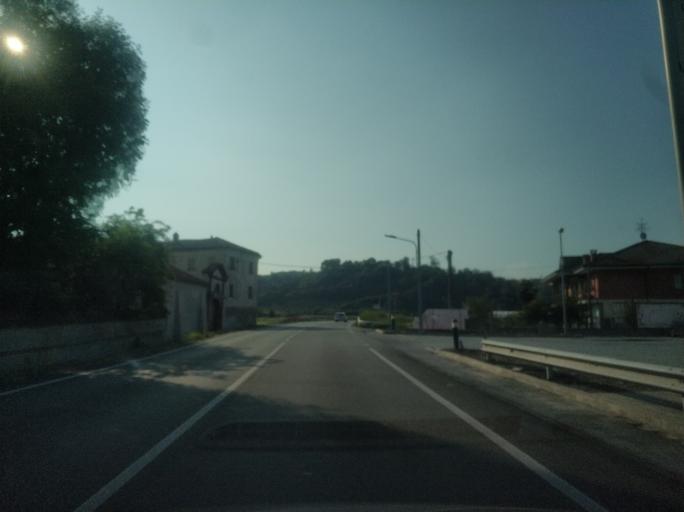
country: IT
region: Piedmont
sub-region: Provincia di Cuneo
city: Roreto
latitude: 44.6670
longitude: 7.8522
